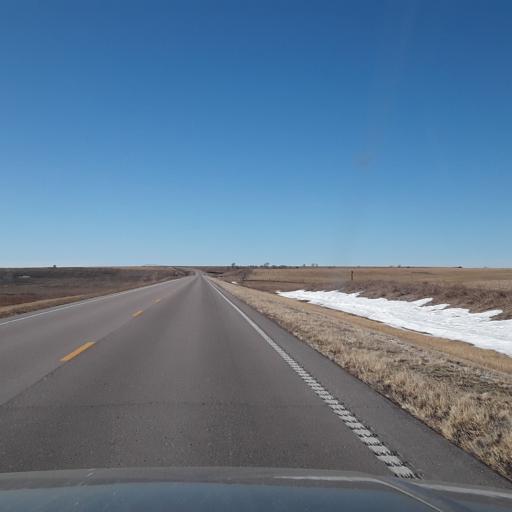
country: US
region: Nebraska
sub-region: Frontier County
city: Stockville
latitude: 40.7057
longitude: -100.2288
